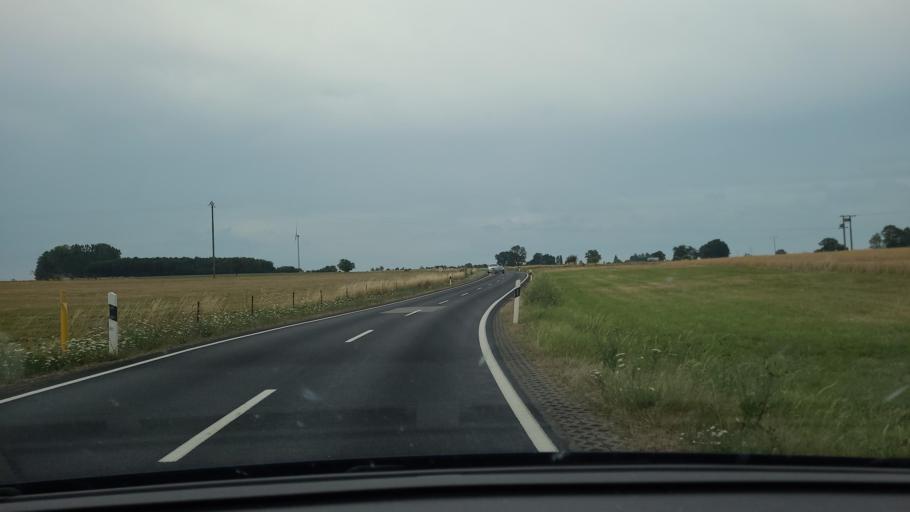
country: LU
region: Luxembourg
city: Hautcharage
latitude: 49.5955
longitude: 5.9140
